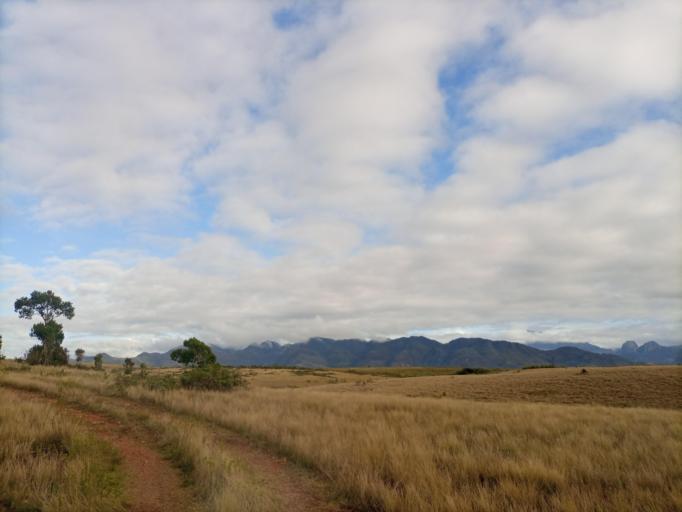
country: MG
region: Anosy
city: Fort Dauphin
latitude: -24.3097
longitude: 47.2448
